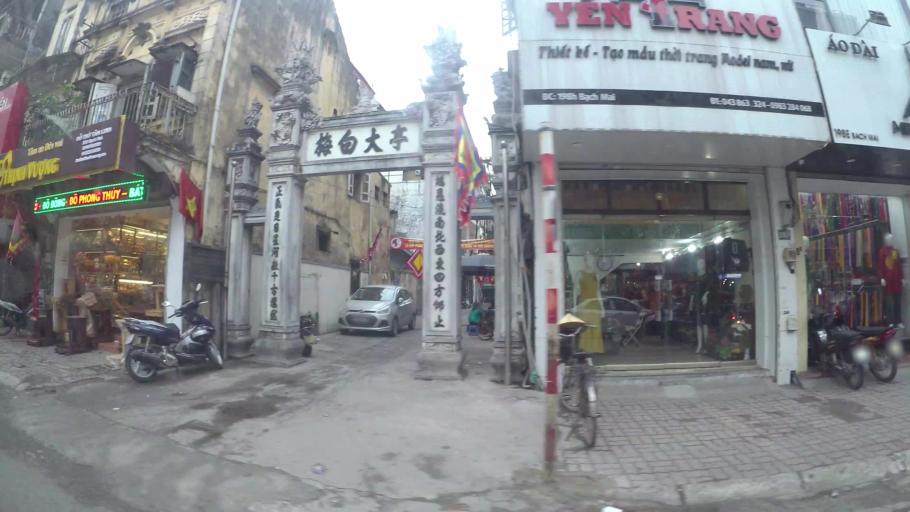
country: VN
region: Ha Noi
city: Hai BaTrung
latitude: 21.0045
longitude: 105.8511
